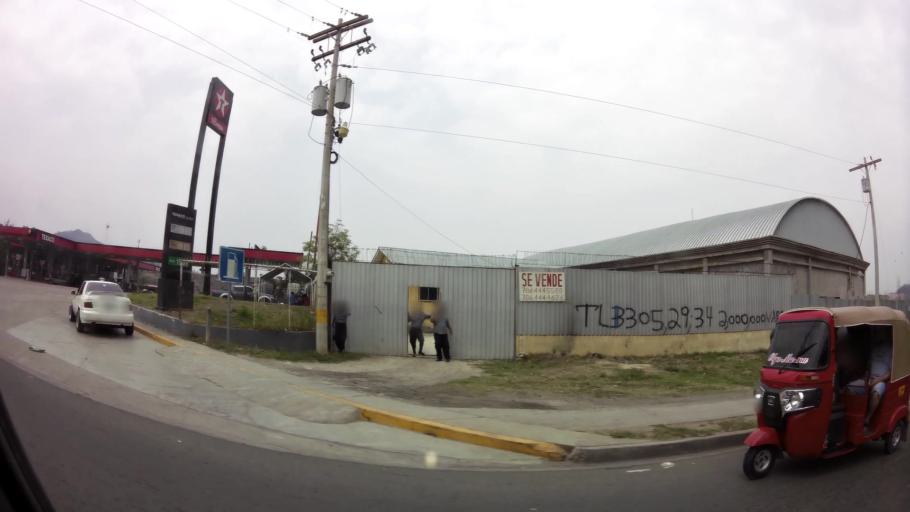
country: HN
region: Francisco Morazan
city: Tegucigalpa
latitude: 14.0572
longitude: -87.2549
